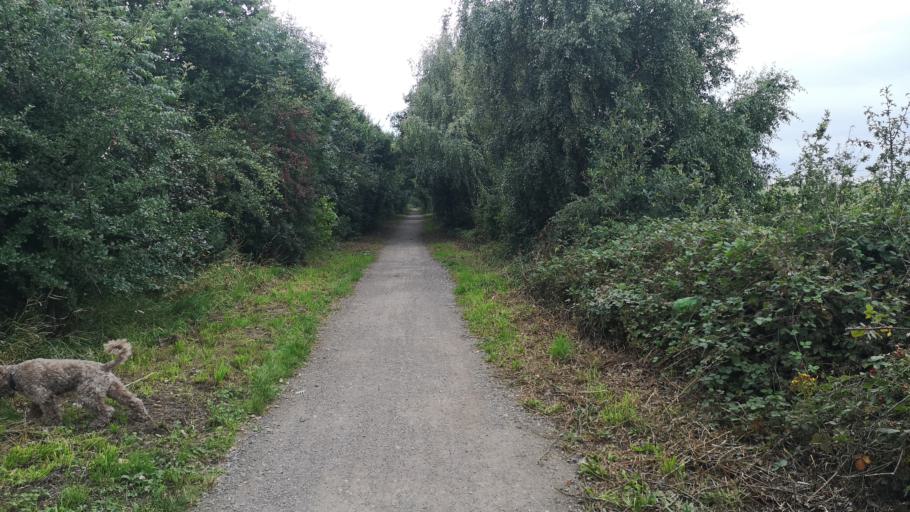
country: GB
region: England
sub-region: City and Borough of Wakefield
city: Notton
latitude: 53.6198
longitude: -1.4668
